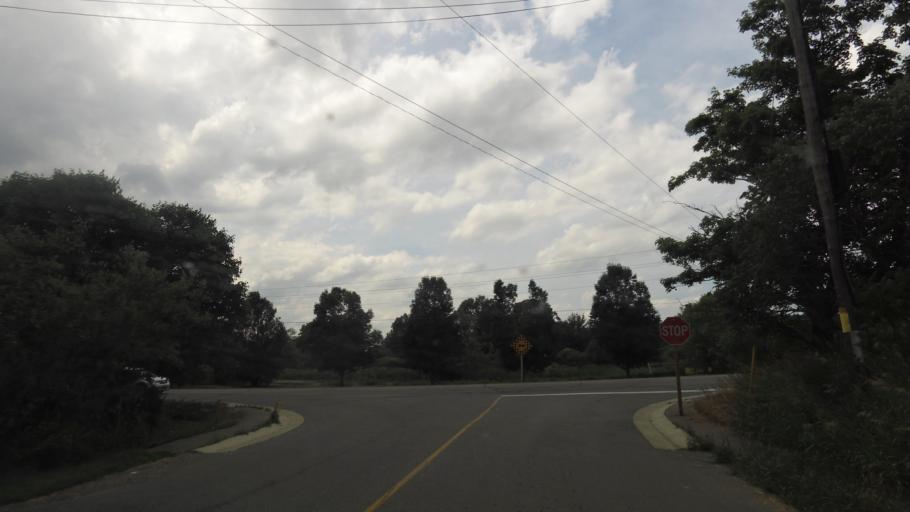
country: CA
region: Ontario
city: Brampton
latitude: 43.8390
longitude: -79.8724
